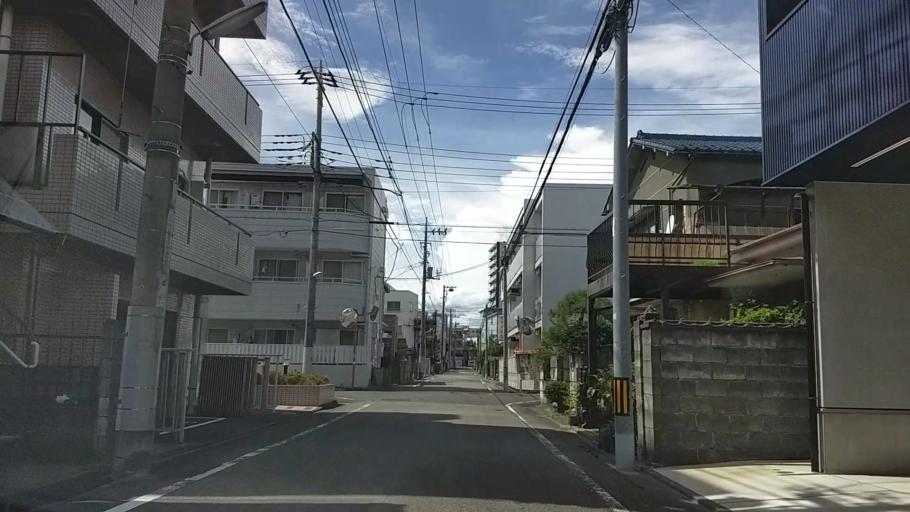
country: JP
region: Tokyo
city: Hachioji
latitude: 35.6589
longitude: 139.3484
